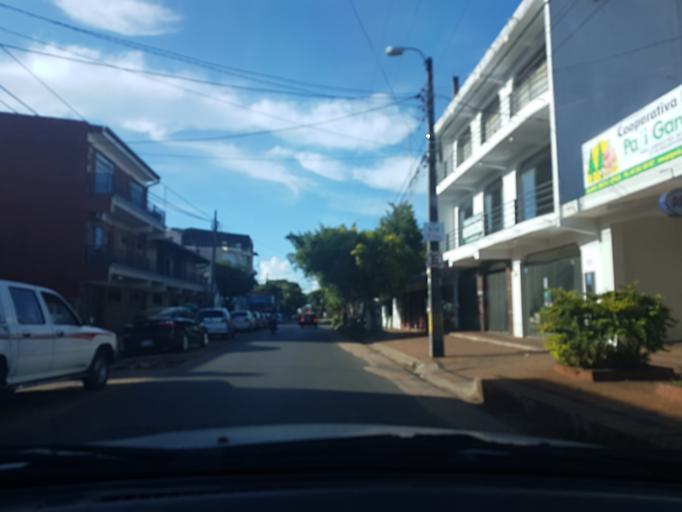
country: PY
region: Central
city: San Lorenzo
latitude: -25.2697
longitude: -57.4916
